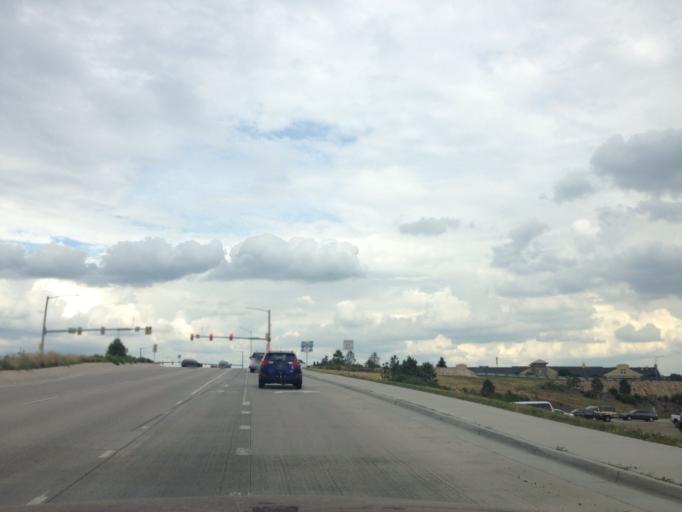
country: US
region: Colorado
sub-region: Weld County
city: Windsor
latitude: 40.4793
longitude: -104.9939
